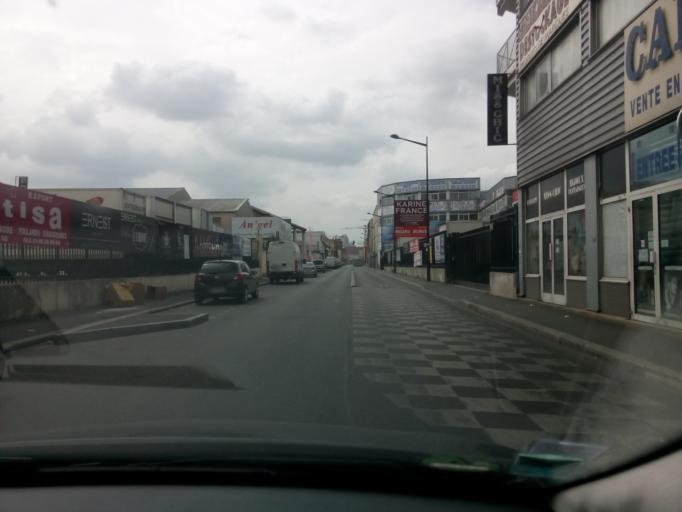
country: FR
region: Ile-de-France
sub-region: Departement de Seine-Saint-Denis
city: Aubervilliers
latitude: 48.9102
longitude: 2.3730
